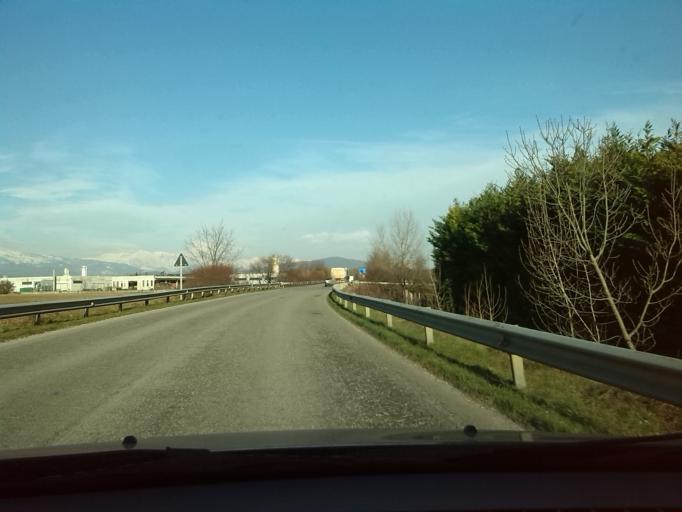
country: IT
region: Friuli Venezia Giulia
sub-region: Provincia di Udine
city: Orsaria
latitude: 46.0193
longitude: 13.3896
